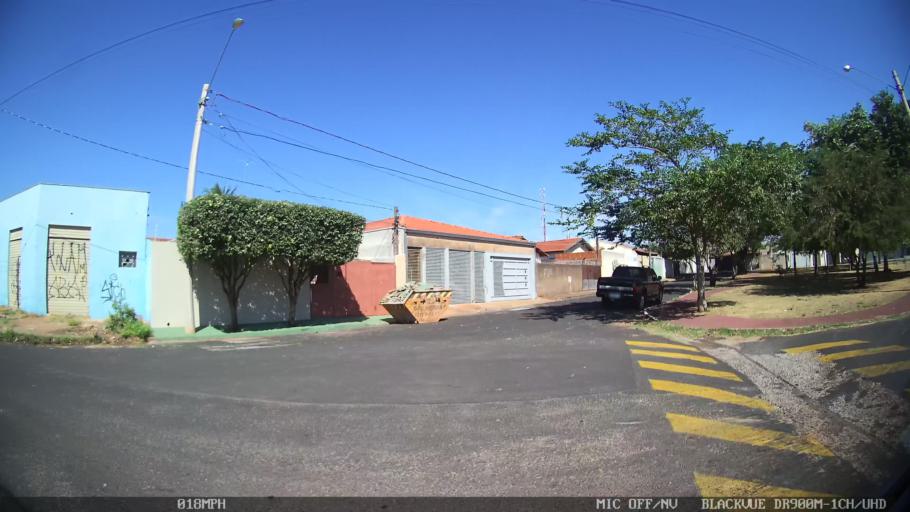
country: BR
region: Sao Paulo
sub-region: Sao Jose Do Rio Preto
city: Sao Jose do Rio Preto
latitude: -20.7661
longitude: -49.4101
